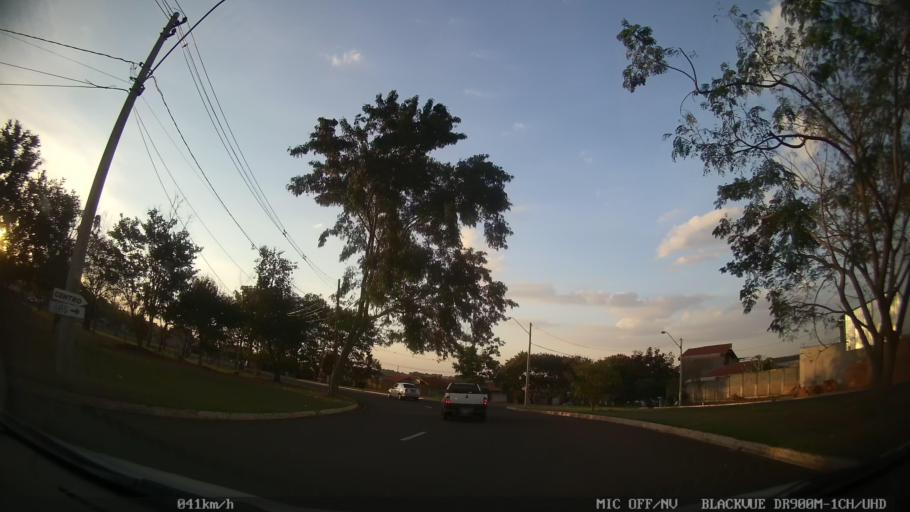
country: BR
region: Sao Paulo
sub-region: Ribeirao Preto
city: Ribeirao Preto
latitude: -21.1468
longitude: -47.8514
